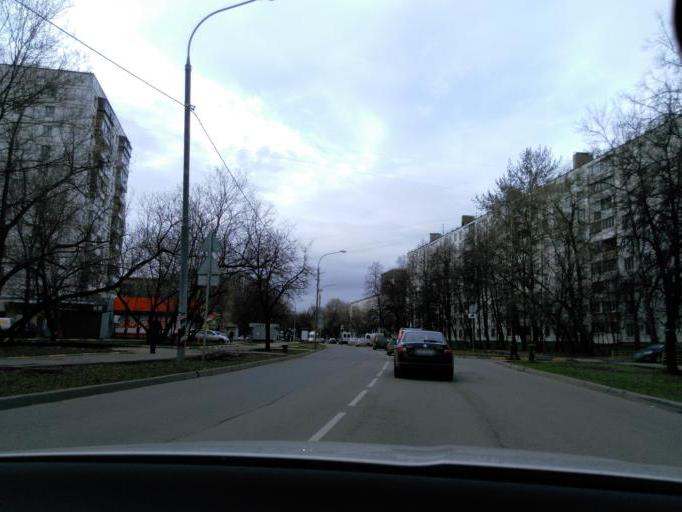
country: RU
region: Moskovskaya
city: Levoberezhnyy
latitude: 55.8474
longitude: 37.4888
